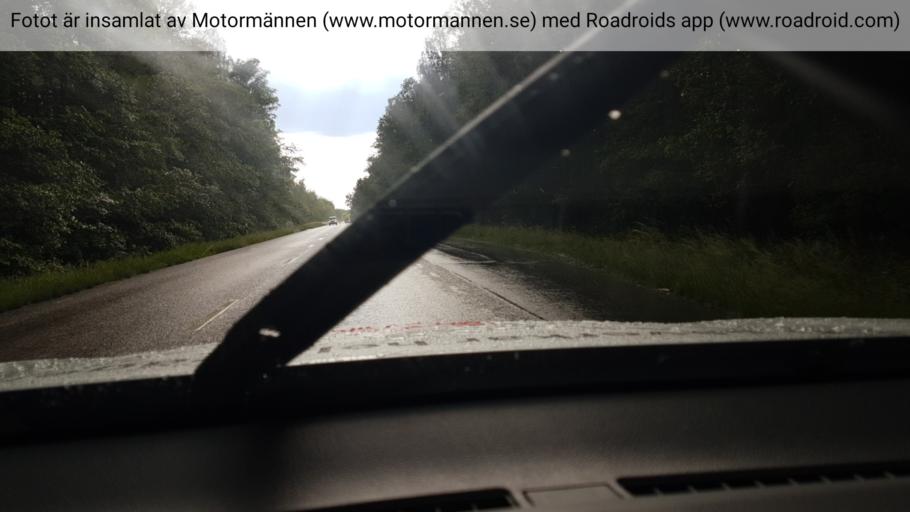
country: SE
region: Vaestra Goetaland
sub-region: Hjo Kommun
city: Hjo
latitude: 58.2349
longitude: 14.2206
